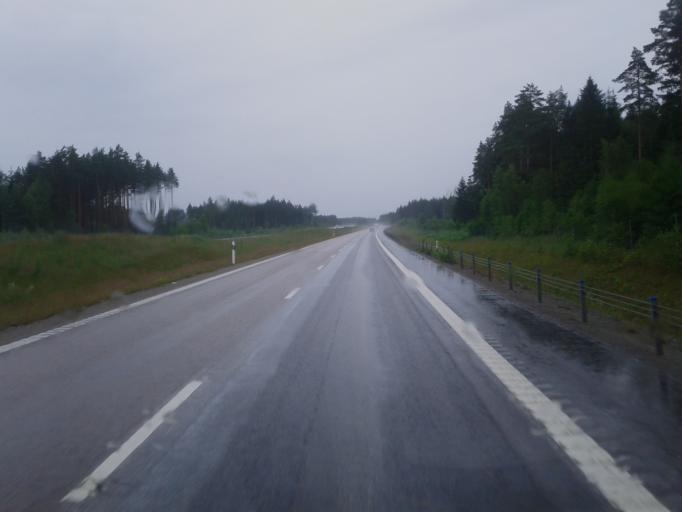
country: SE
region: Uppsala
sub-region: Tierps Kommun
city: Tierp
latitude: 60.2624
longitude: 17.5007
